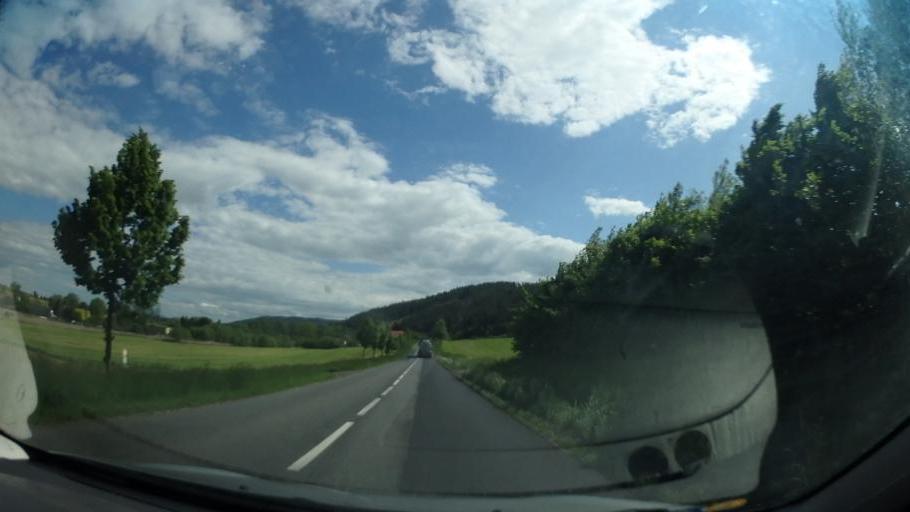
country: CZ
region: Pardubicky
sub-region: Okres Svitavy
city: Moravska Trebova
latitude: 49.7398
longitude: 16.6495
